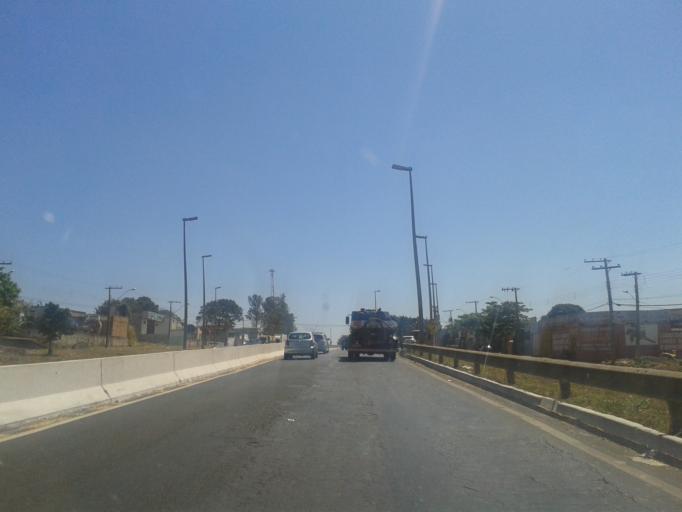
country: BR
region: Minas Gerais
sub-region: Uberlandia
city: Uberlandia
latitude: -18.9070
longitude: -48.3168
